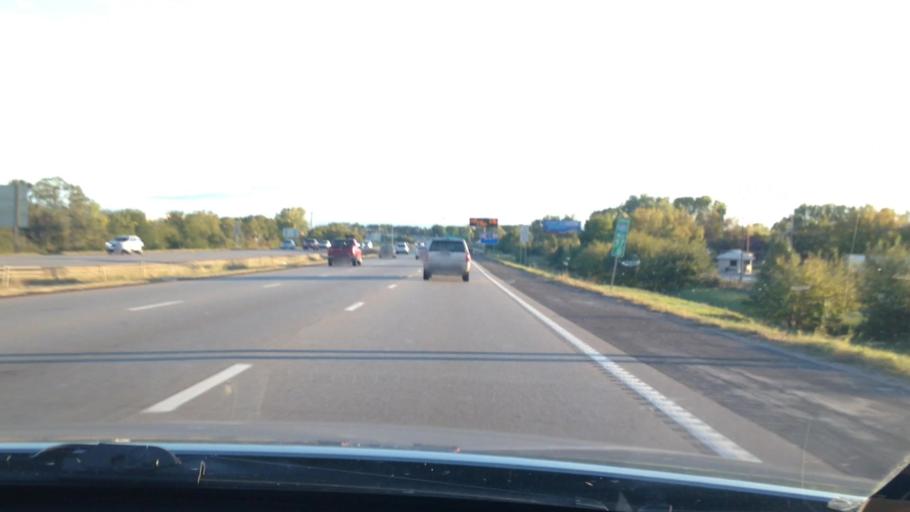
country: US
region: Missouri
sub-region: Clay County
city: Claycomo
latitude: 39.1406
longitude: -94.4989
